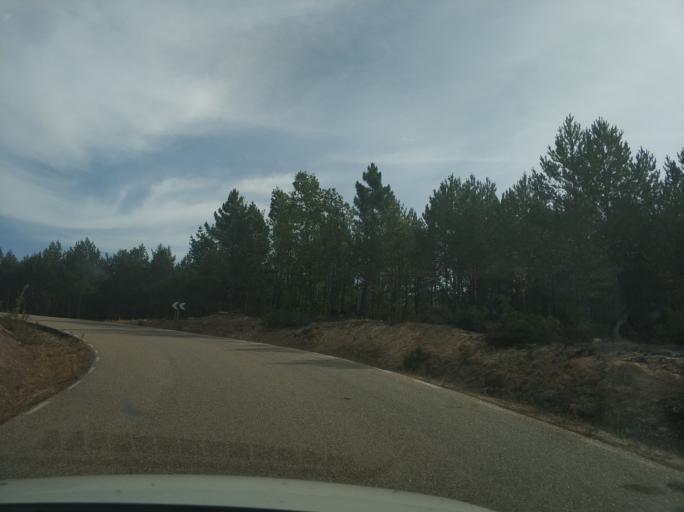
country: ES
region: Castille and Leon
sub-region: Provincia de Soria
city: Duruelo de la Sierra
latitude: 41.8803
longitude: -2.9364
